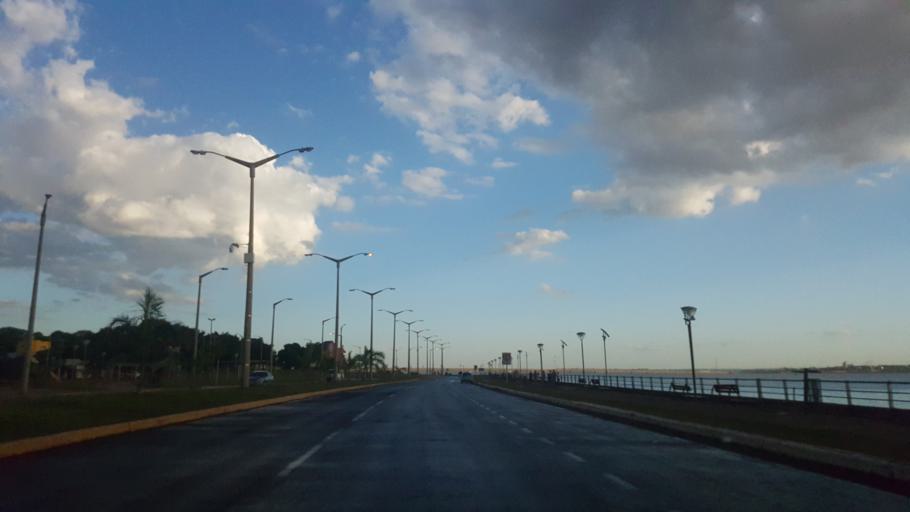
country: PY
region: Itapua
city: Encarnacion
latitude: -27.3508
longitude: -55.8676
